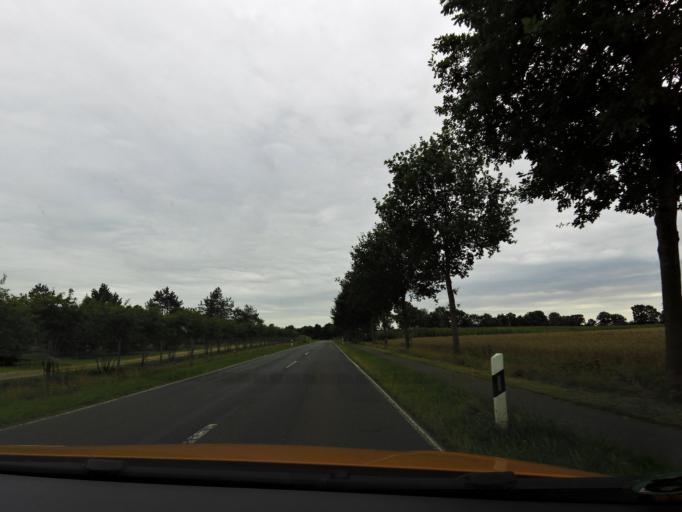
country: DE
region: Lower Saxony
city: Wiefelstede
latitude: 53.2095
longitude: 8.0925
